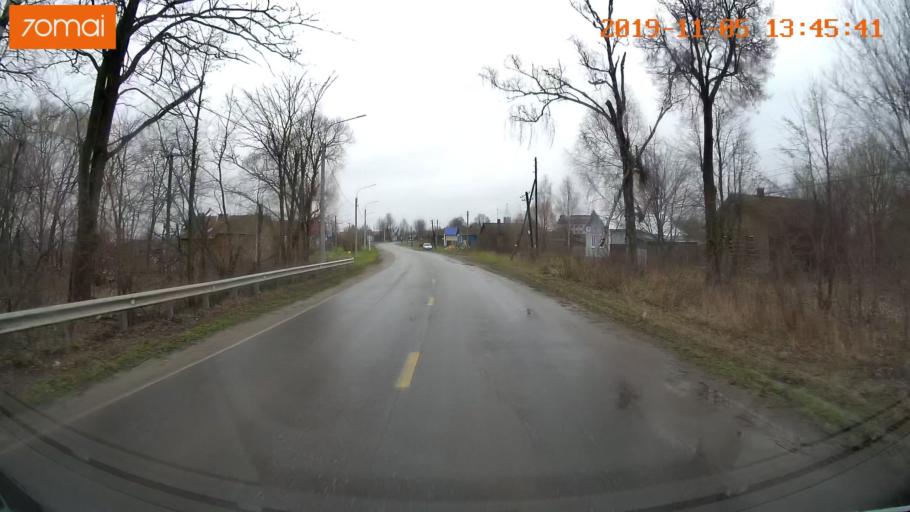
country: RU
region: Ivanovo
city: Shuya
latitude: 56.9906
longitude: 41.4120
